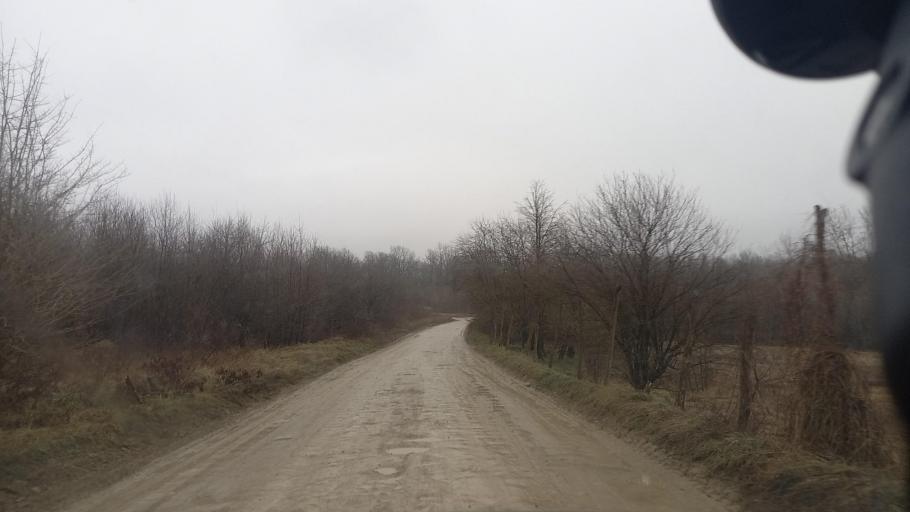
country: RU
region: Krasnodarskiy
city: Saratovskaya
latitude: 44.6659
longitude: 39.2193
